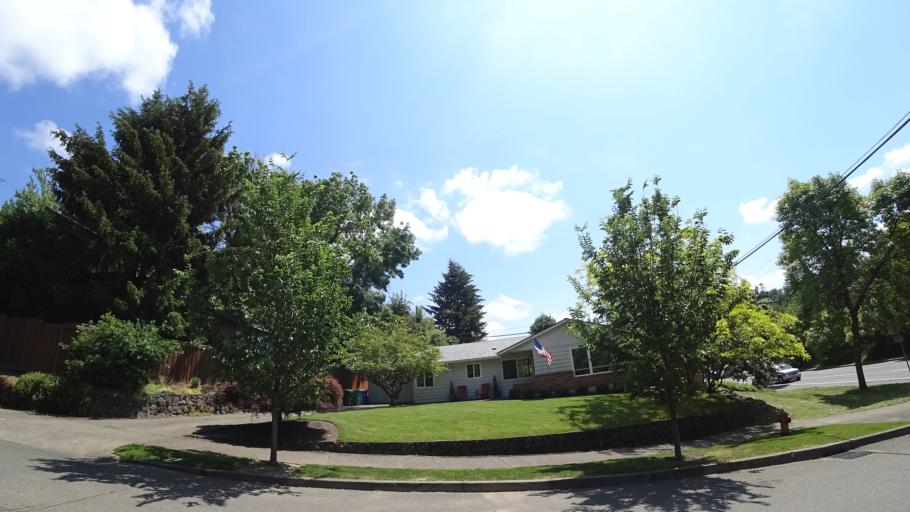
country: US
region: Oregon
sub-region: Multnomah County
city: Portland
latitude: 45.4727
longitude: -122.6944
